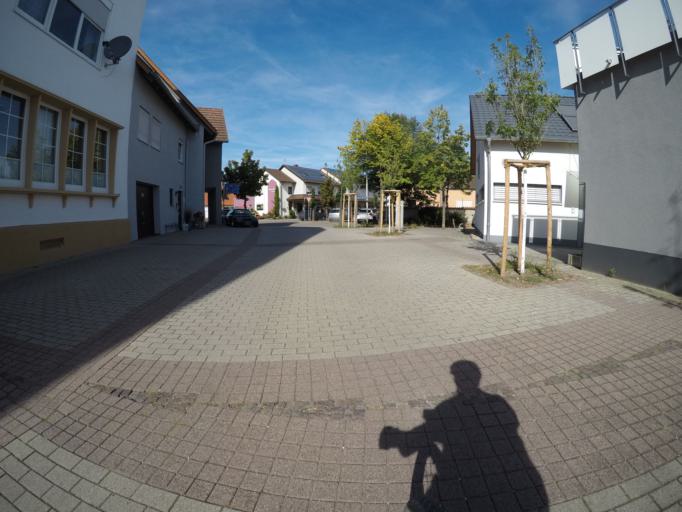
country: DE
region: Baden-Wuerttemberg
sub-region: Karlsruhe Region
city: Ubstadt-Weiher
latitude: 49.1794
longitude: 8.6236
